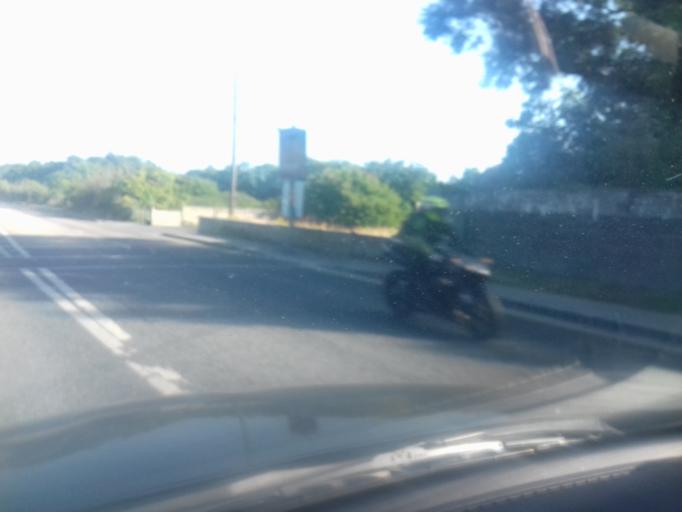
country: IE
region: Leinster
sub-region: An Mhi
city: Ashbourne
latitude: 53.4621
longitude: -6.3532
